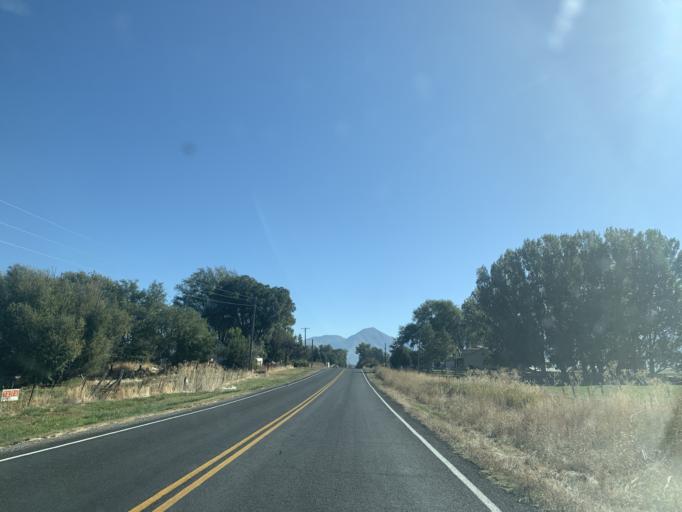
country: US
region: Utah
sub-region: Utah County
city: West Mountain
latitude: 40.0410
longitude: -111.7776
